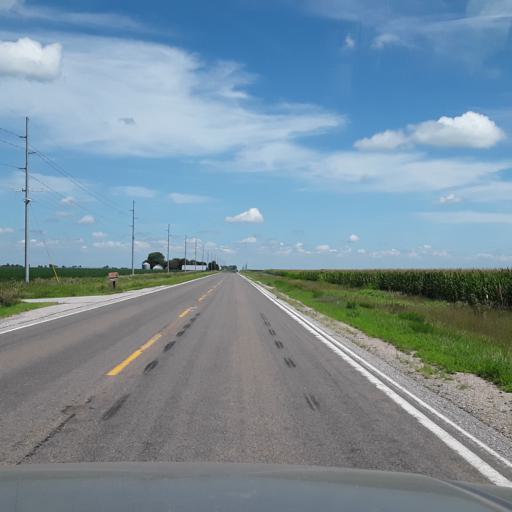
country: US
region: Nebraska
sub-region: York County
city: York
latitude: 40.9195
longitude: -97.4062
